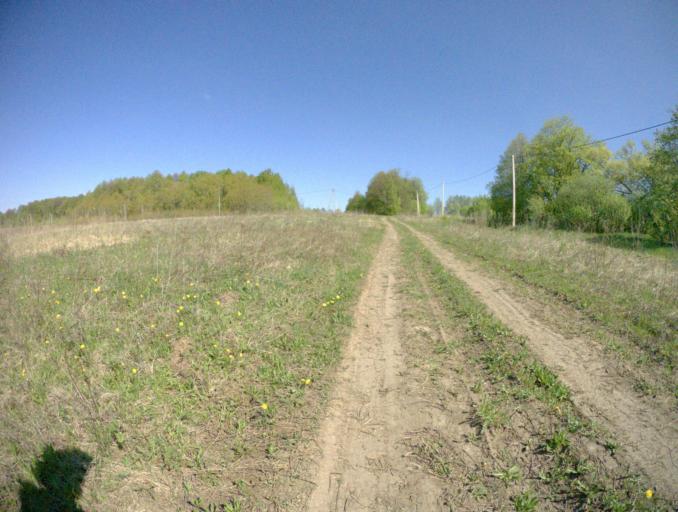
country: RU
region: Vladimir
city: Suzdal'
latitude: 56.2927
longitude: 40.3620
